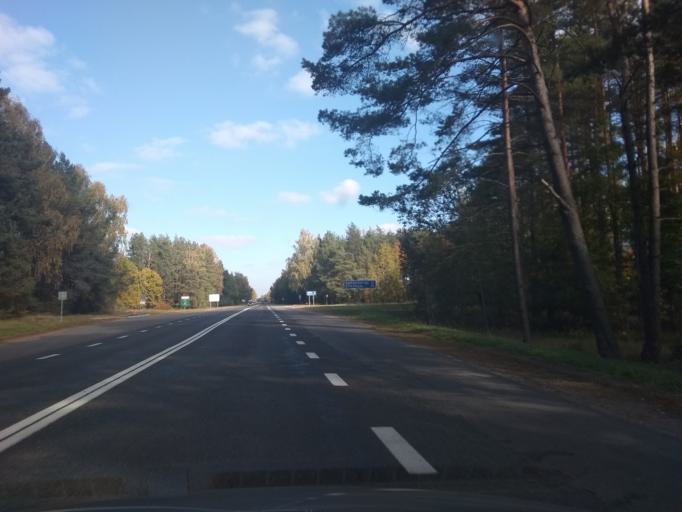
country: BY
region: Brest
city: Baranovichi
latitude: 53.0544
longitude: 25.8613
